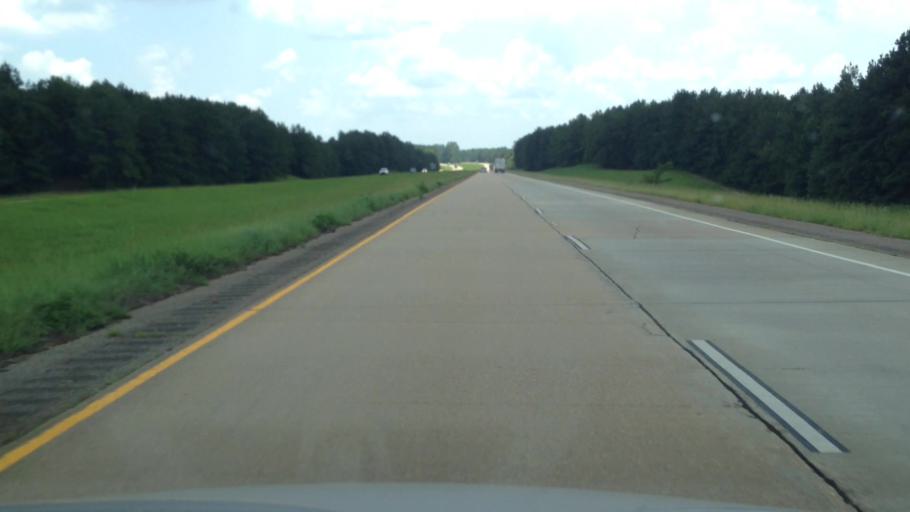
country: US
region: Louisiana
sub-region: Rapides Parish
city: Lecompte
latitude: 31.0480
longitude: -92.4204
